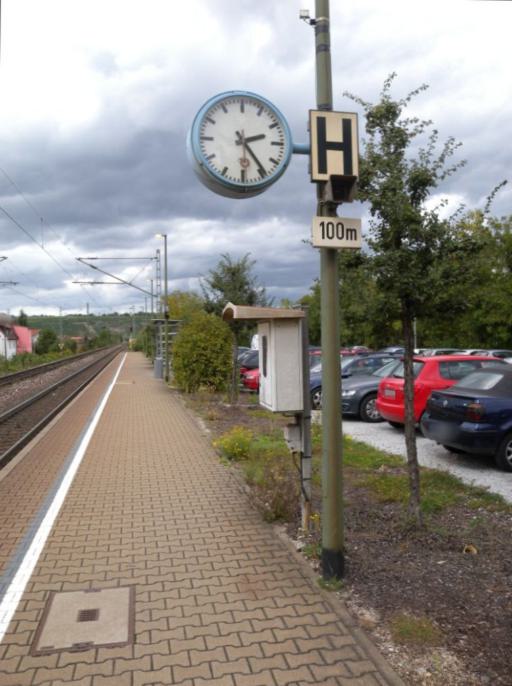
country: DE
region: Baden-Wuerttemberg
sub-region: Regierungsbezirk Stuttgart
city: Kirchheim am Neckar
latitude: 49.0385
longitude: 9.1508
